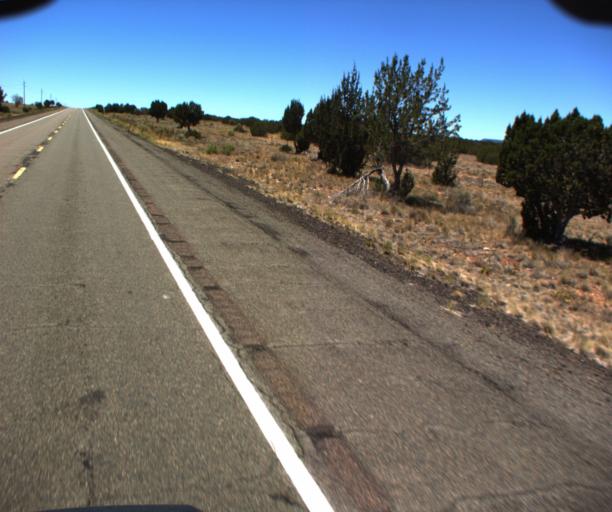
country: US
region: Arizona
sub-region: Coconino County
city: LeChee
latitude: 34.8049
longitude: -110.9771
